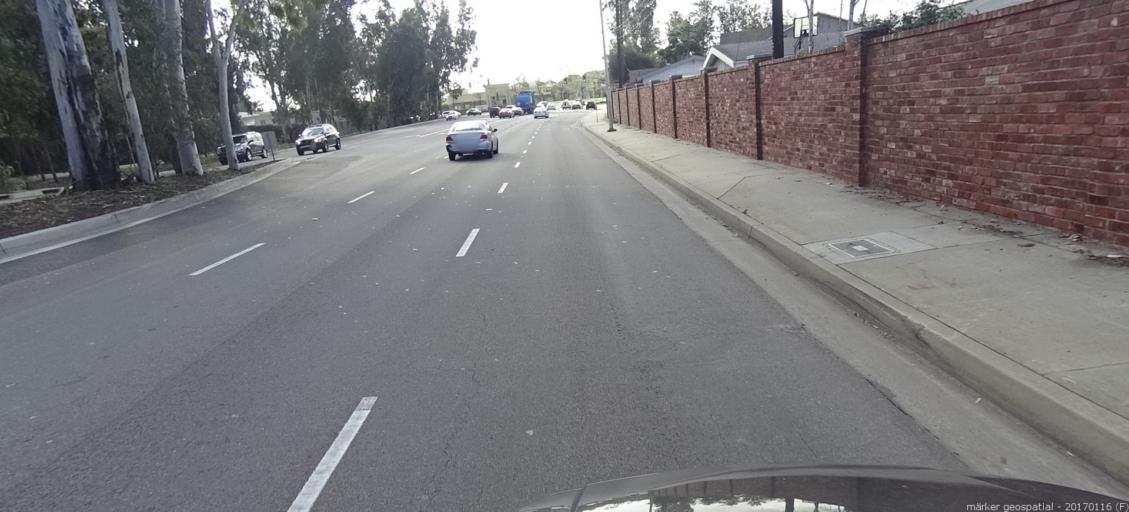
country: US
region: California
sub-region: Orange County
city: Rossmoor
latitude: 33.7795
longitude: -118.0722
